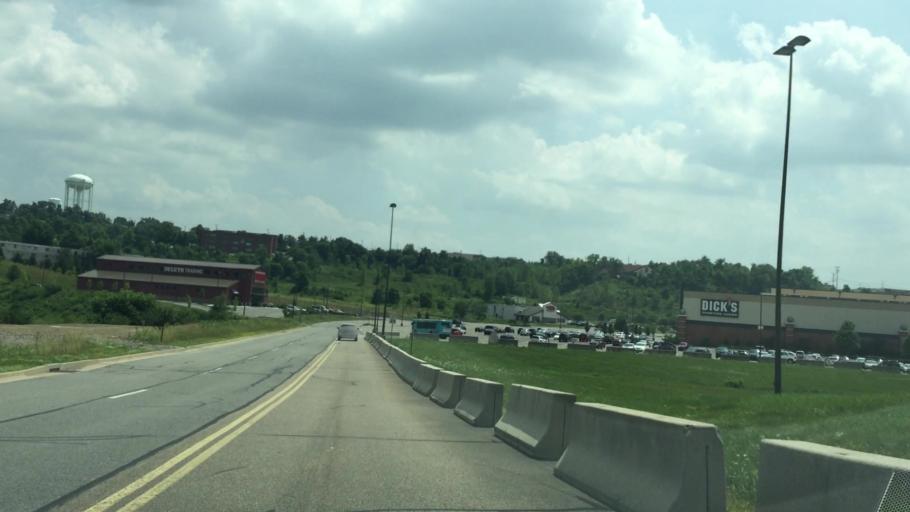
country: US
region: Pennsylvania
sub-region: Allegheny County
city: Rennerdale
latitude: 40.4551
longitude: -80.1550
